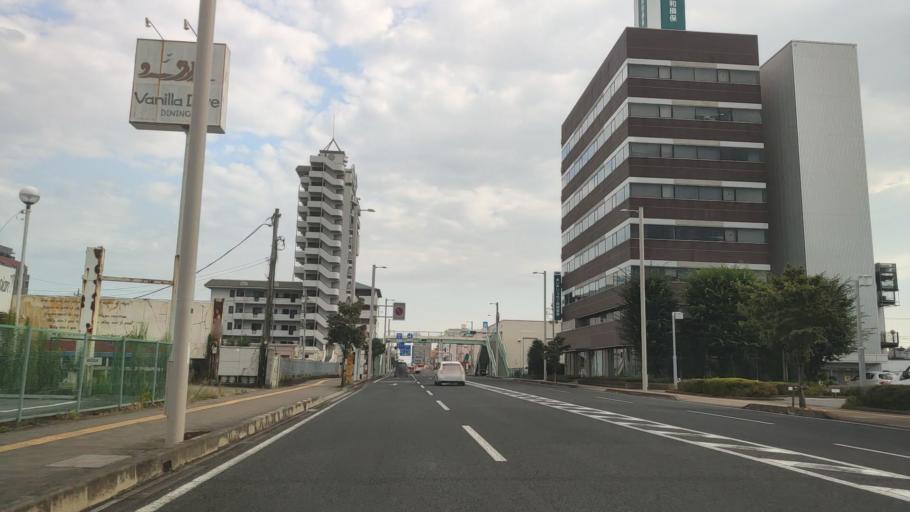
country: JP
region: Tochigi
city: Utsunomiya-shi
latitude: 36.5537
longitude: 139.8795
